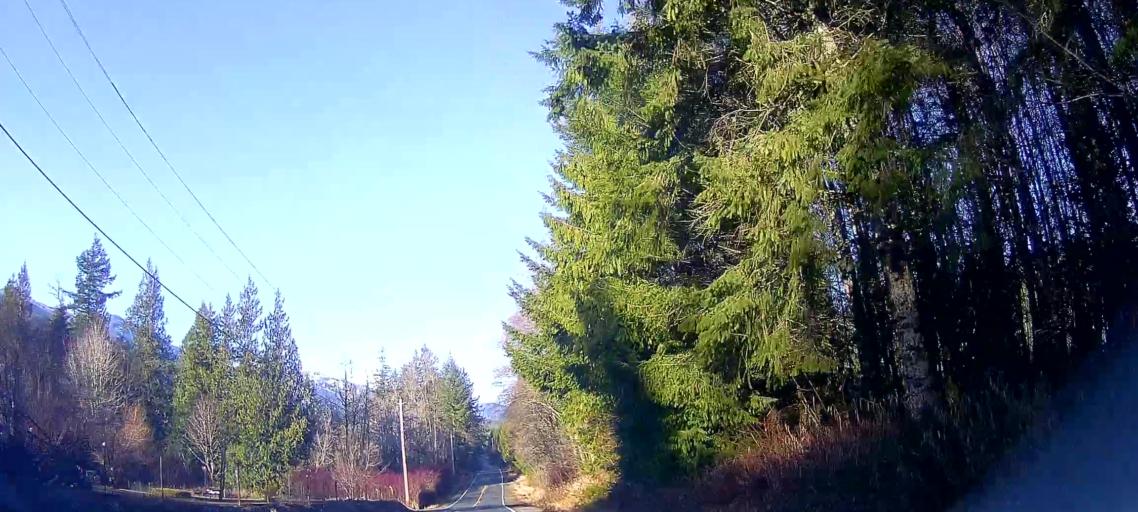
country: US
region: Washington
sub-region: Snohomish County
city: Darrington
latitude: 48.5565
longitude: -121.7658
